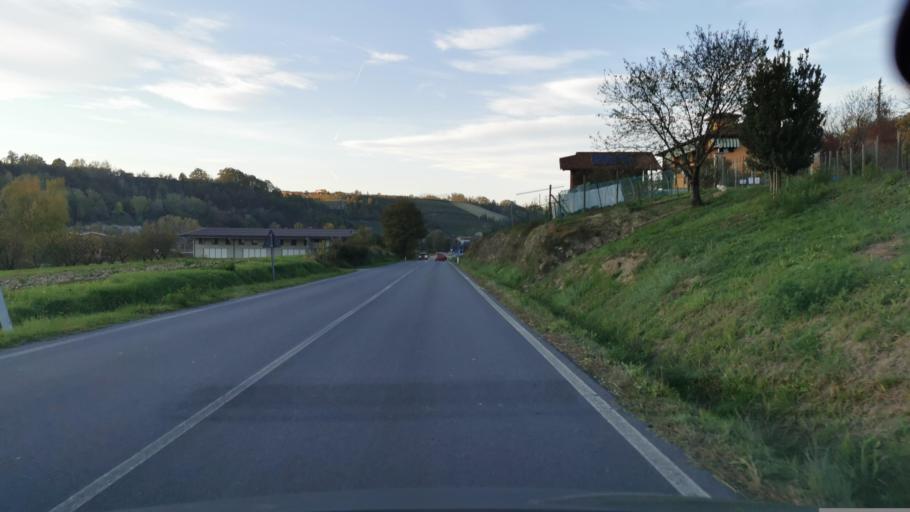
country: IT
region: Piedmont
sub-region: Provincia di Cuneo
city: Dogliani
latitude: 44.5450
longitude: 7.9261
